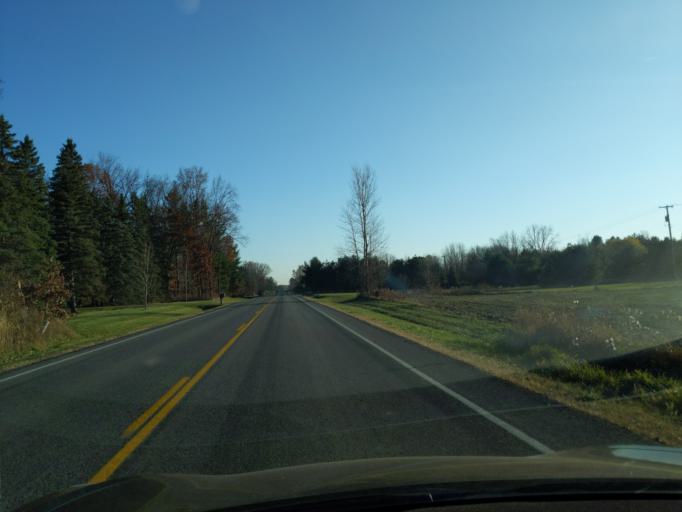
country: US
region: Michigan
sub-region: Ingham County
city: Williamston
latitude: 42.7218
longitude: -84.3156
